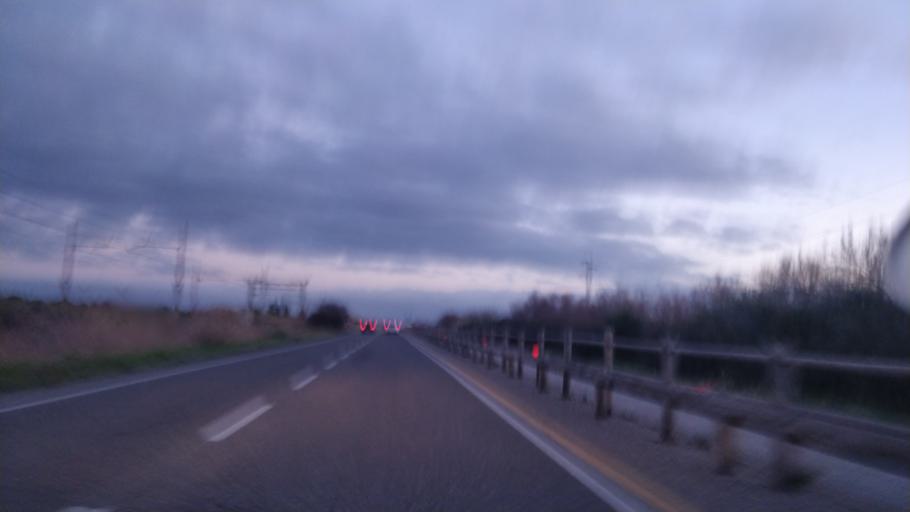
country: IT
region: Tuscany
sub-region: Provincia di Livorno
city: Rosignano Solvay-Castiglioncello
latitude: 43.3786
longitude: 10.4451
